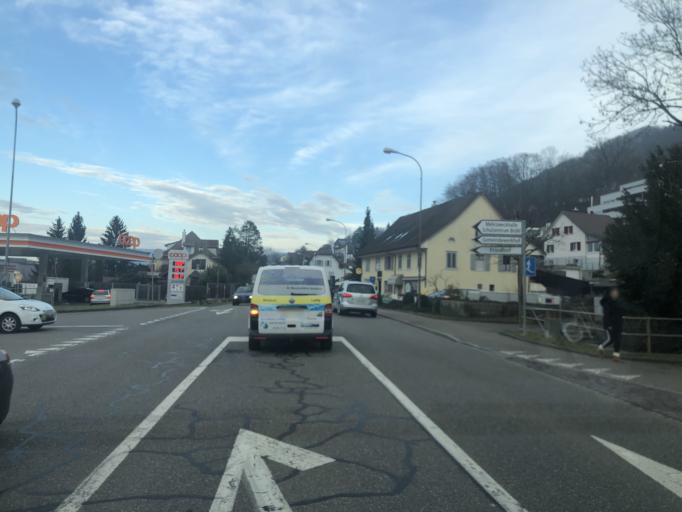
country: CH
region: Aargau
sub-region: Bezirk Baden
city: Gebenstorf
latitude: 47.4829
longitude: 8.2412
